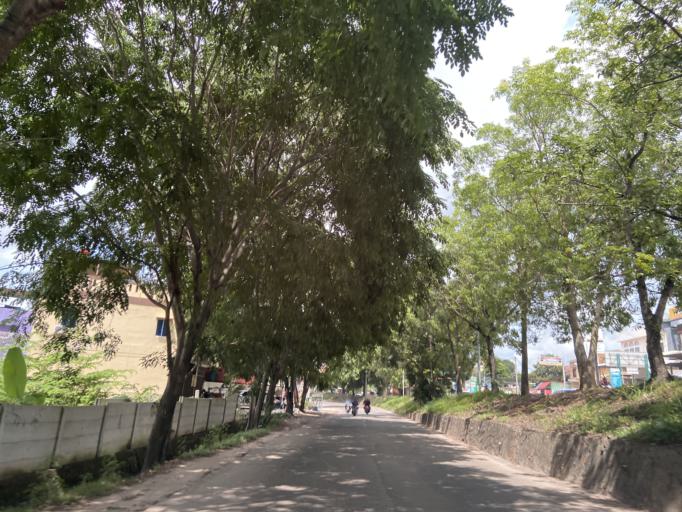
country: SG
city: Singapore
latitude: 1.1361
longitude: 104.0023
